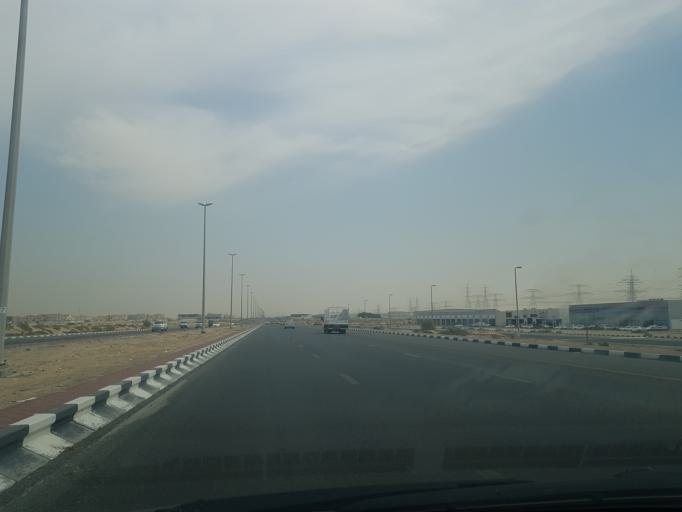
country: AE
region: Ash Shariqah
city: Sharjah
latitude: 25.2564
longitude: 55.5186
